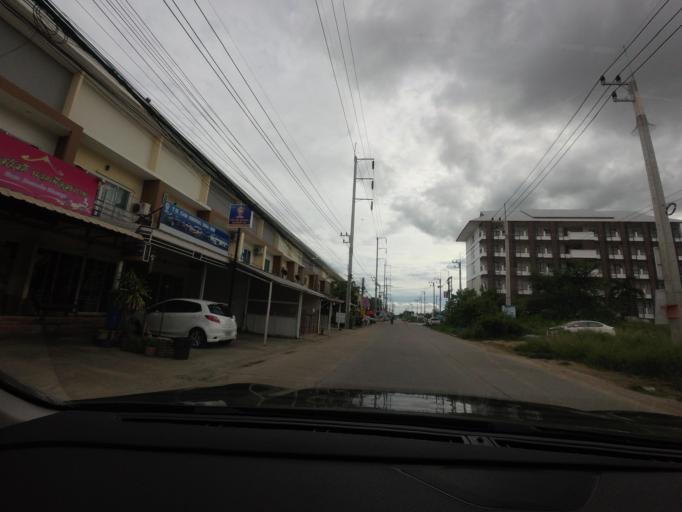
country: TH
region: Prachuap Khiri Khan
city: Hua Hin
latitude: 12.5420
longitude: 99.9505
